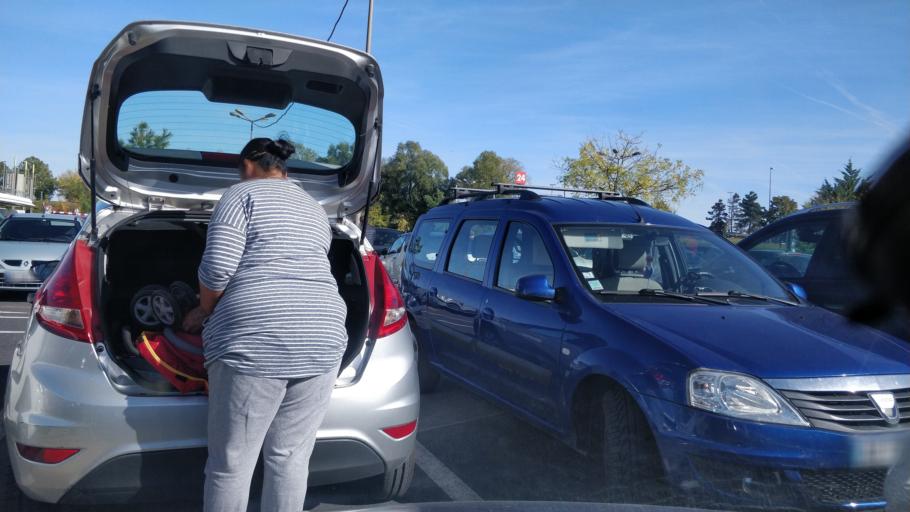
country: FR
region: Ile-de-France
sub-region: Departement de Seine-et-Marne
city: Claye-Souilly
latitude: 48.9451
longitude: 2.6646
